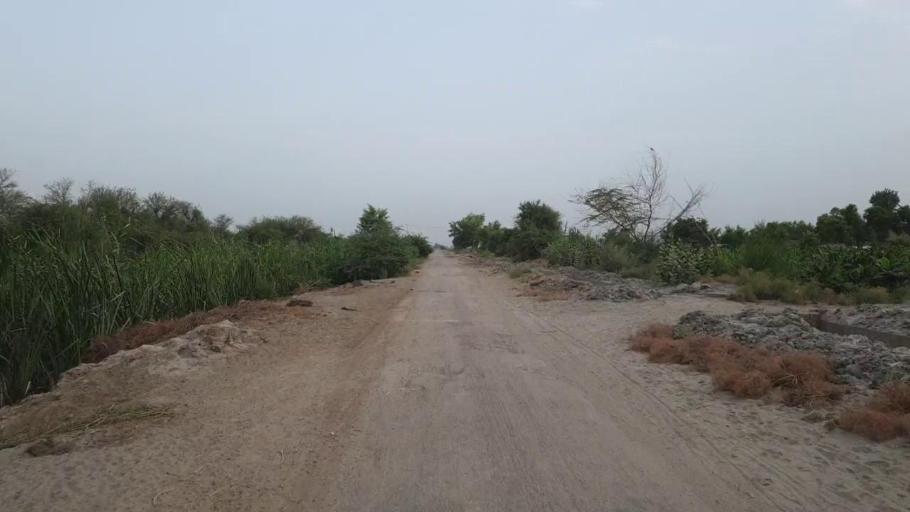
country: PK
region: Sindh
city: Daur
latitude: 26.4179
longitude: 68.2251
